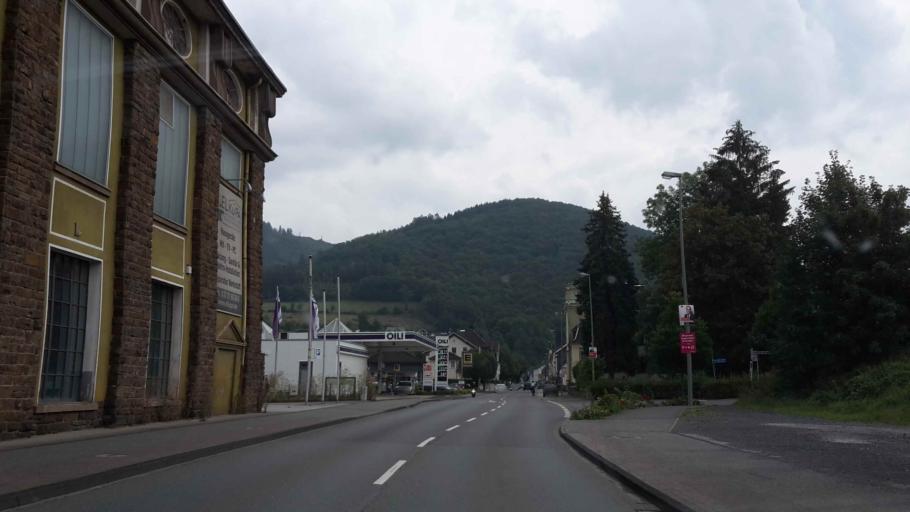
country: DE
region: North Rhine-Westphalia
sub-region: Regierungsbezirk Arnsberg
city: Lennestadt
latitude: 51.1254
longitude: 8.0625
